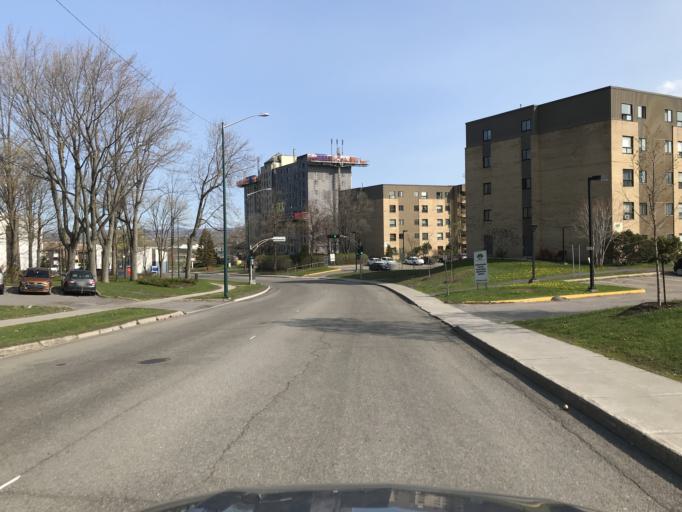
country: CA
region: Quebec
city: L'Ancienne-Lorette
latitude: 46.7887
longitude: -71.2819
